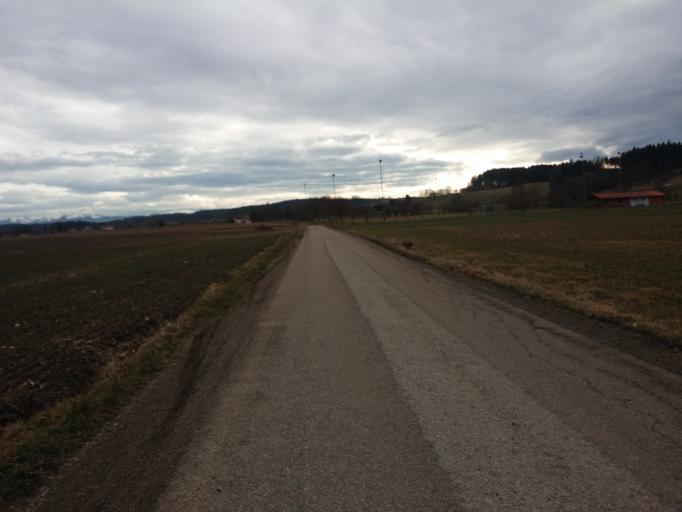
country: DE
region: Bavaria
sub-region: Upper Bavaria
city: Glonn
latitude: 47.9988
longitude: 11.8623
